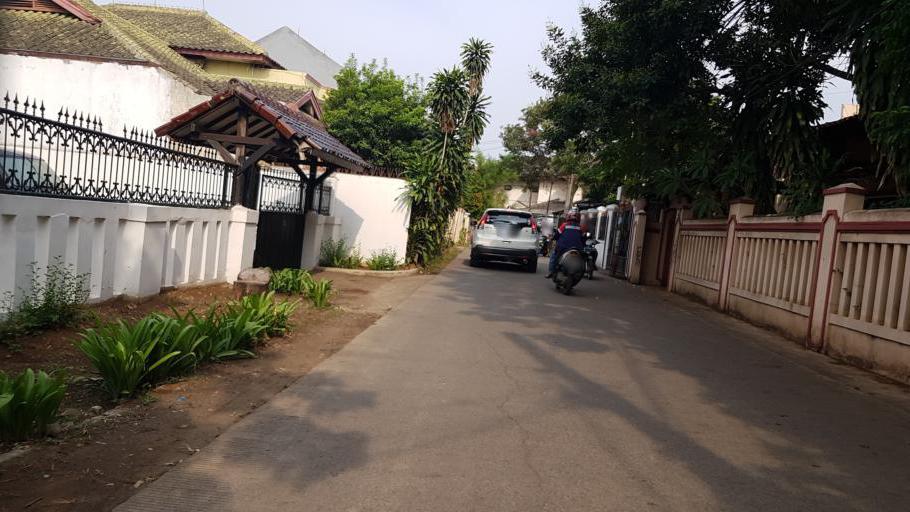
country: ID
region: West Java
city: Pamulang
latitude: -6.3256
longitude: 106.7976
